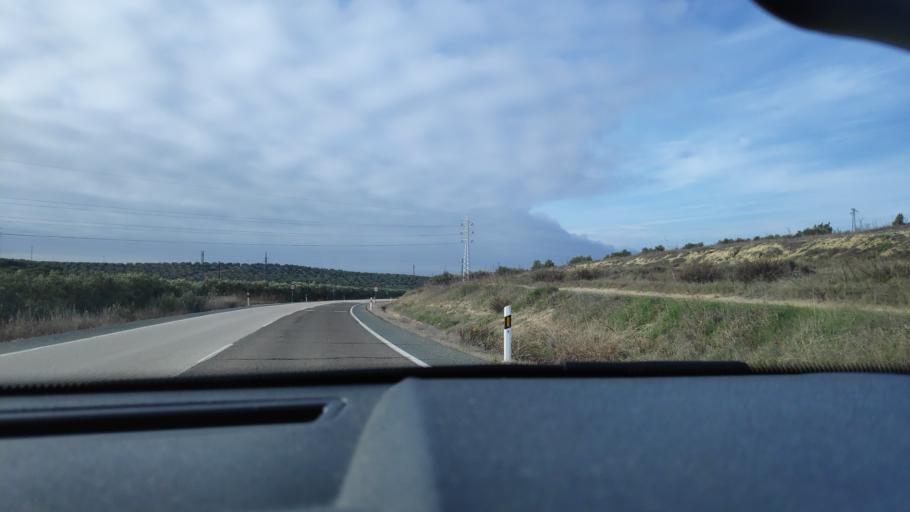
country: ES
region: Andalusia
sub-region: Provincia de Jaen
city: Linares
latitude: 38.0806
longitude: -3.6351
